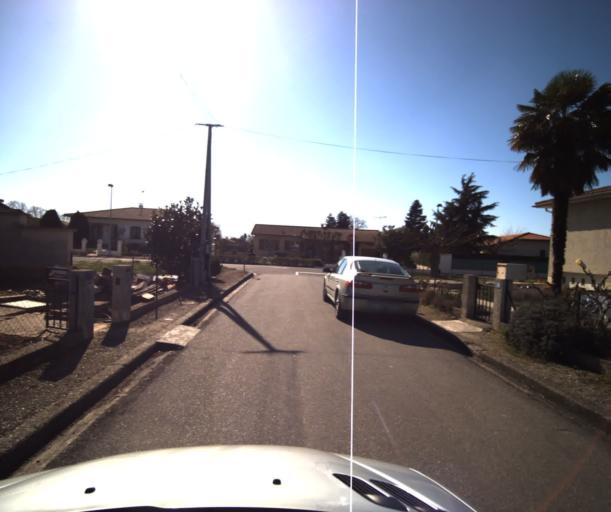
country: FR
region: Midi-Pyrenees
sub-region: Departement du Tarn-et-Garonne
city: Bressols
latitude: 43.9692
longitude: 1.3374
